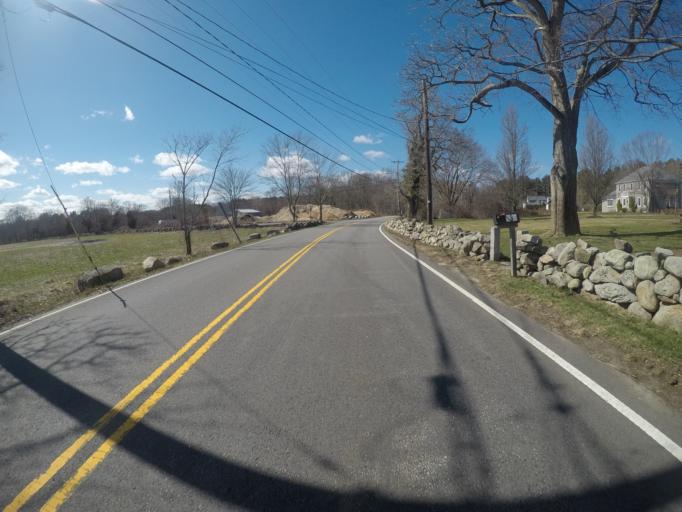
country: US
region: Massachusetts
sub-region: Bristol County
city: Easton
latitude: 42.0393
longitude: -71.1388
